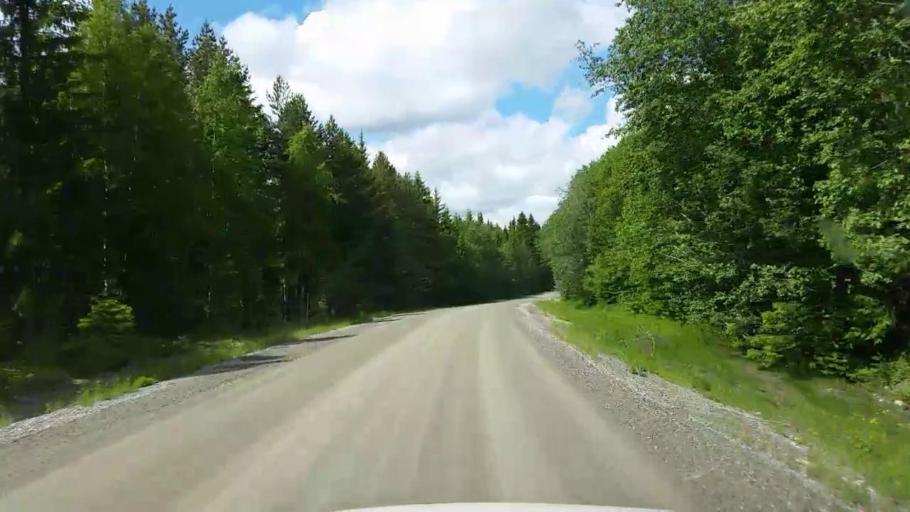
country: SE
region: Gaevleborg
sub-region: Bollnas Kommun
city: Vittsjo
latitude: 61.0454
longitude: 16.3386
